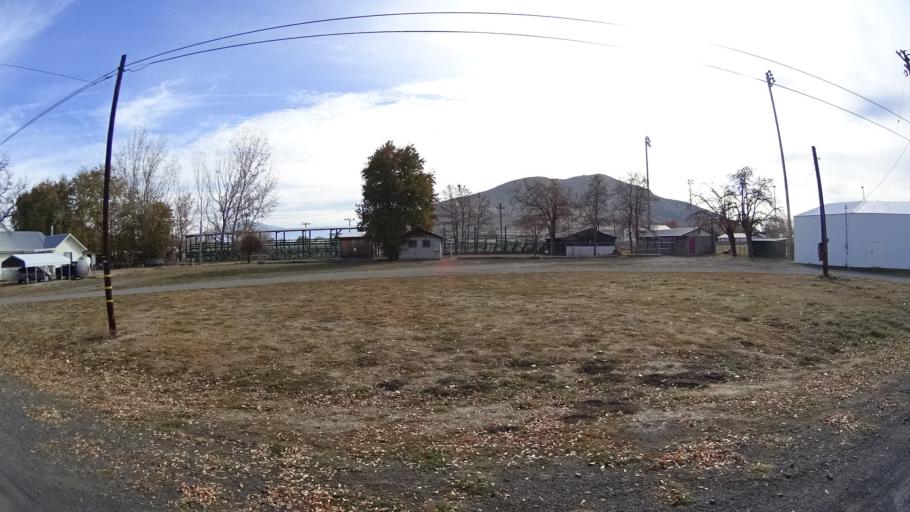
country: US
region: California
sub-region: Siskiyou County
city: Montague
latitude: 41.7236
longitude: -122.5270
